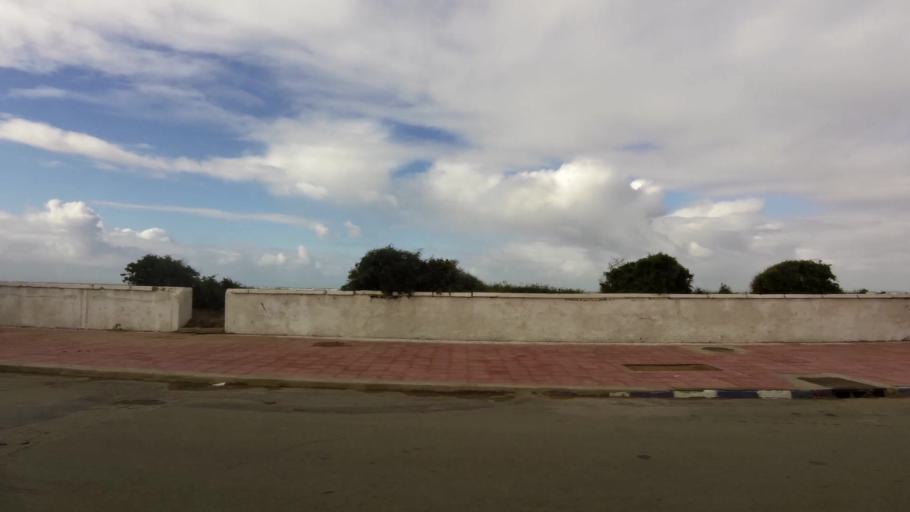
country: MA
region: Doukkala-Abda
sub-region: El-Jadida
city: El Jadida
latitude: 33.2443
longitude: -8.4770
